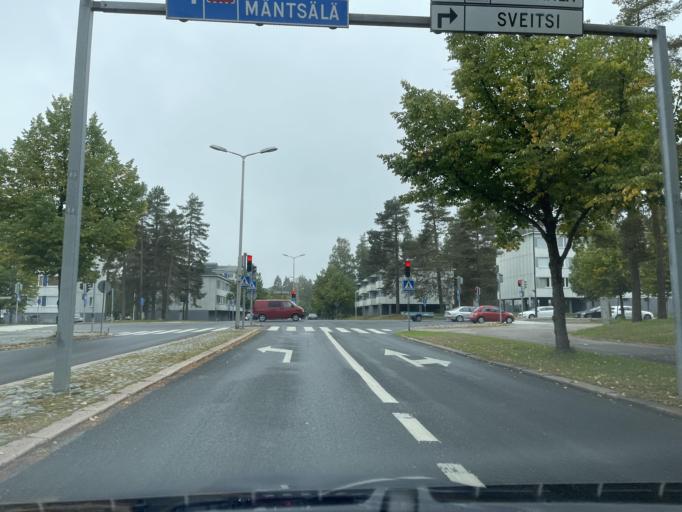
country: FI
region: Uusimaa
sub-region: Helsinki
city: Hyvinge
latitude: 60.6213
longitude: 24.8466
